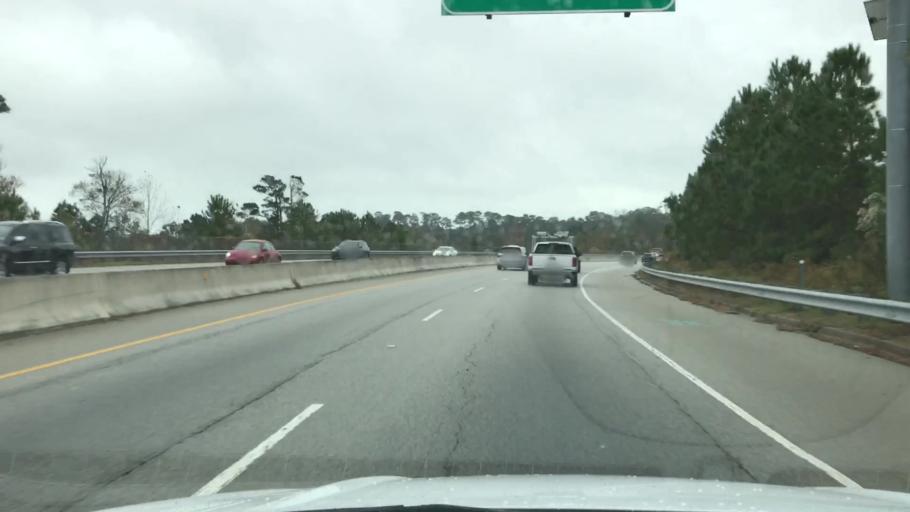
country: US
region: South Carolina
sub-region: Horry County
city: Myrtle Beach
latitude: 33.7489
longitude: -78.8485
